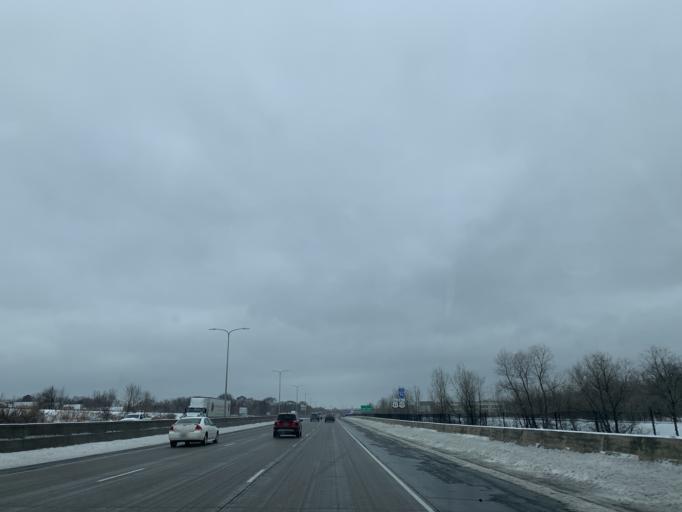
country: US
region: Minnesota
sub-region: Washington County
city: Newport
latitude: 44.8584
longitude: -92.9954
